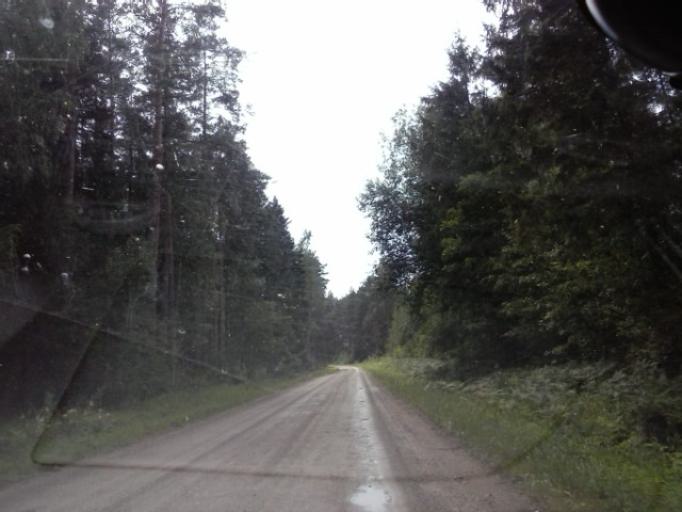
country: EE
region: Polvamaa
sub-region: Polva linn
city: Polva
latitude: 58.2558
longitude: 26.9861
